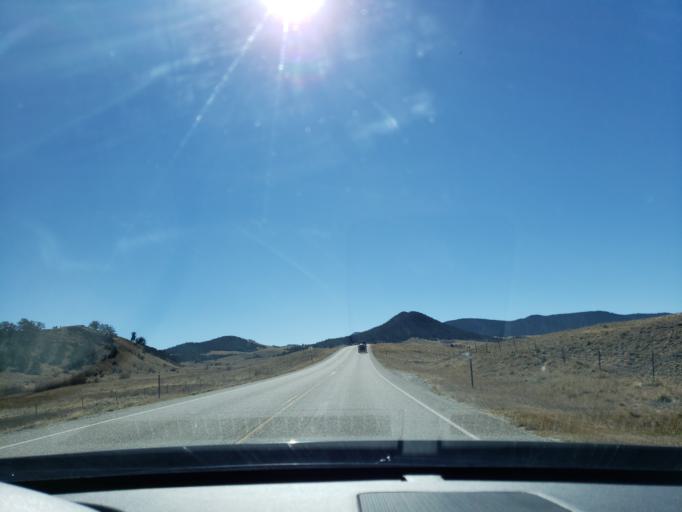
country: US
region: Colorado
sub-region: Chaffee County
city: Salida
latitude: 38.8579
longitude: -105.6539
